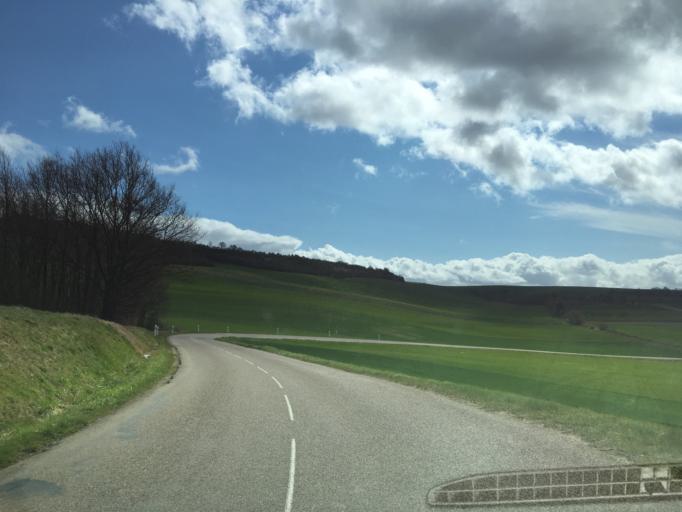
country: FR
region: Bourgogne
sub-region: Departement de l'Yonne
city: Pourrain
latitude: 47.7941
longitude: 3.4075
